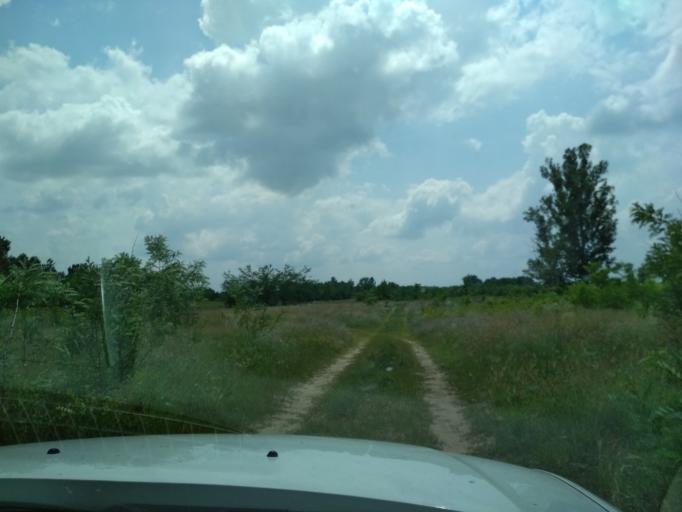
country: HU
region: Pest
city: Tapioszentmarton
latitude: 47.3727
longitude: 19.7663
